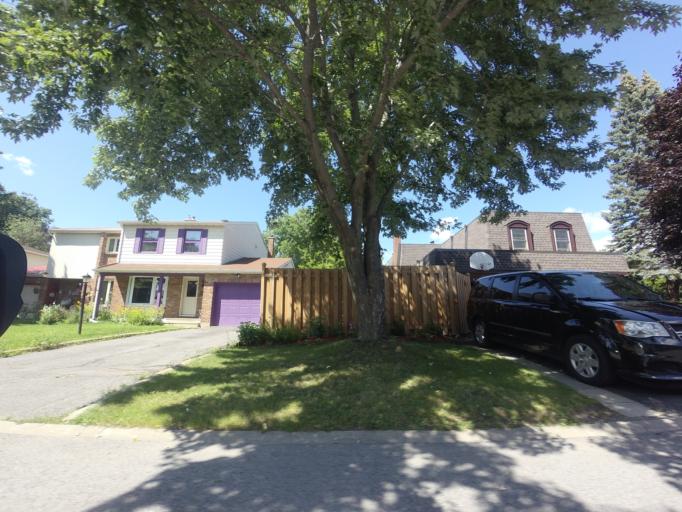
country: CA
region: Ontario
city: Bells Corners
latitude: 45.3286
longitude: -75.7768
